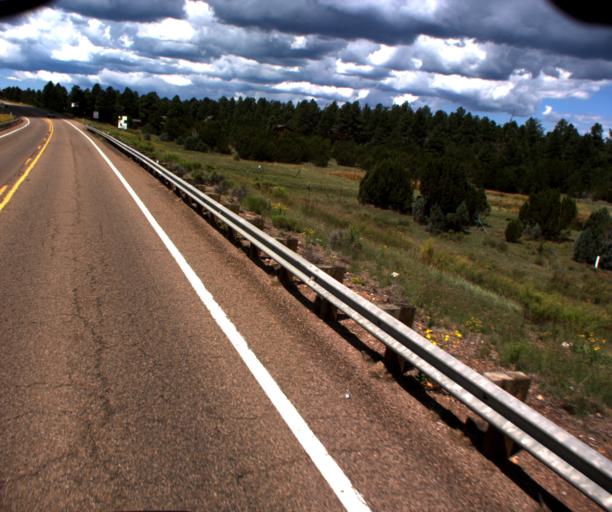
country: US
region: Arizona
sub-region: Navajo County
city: Heber-Overgaard
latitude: 34.3936
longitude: -110.5220
